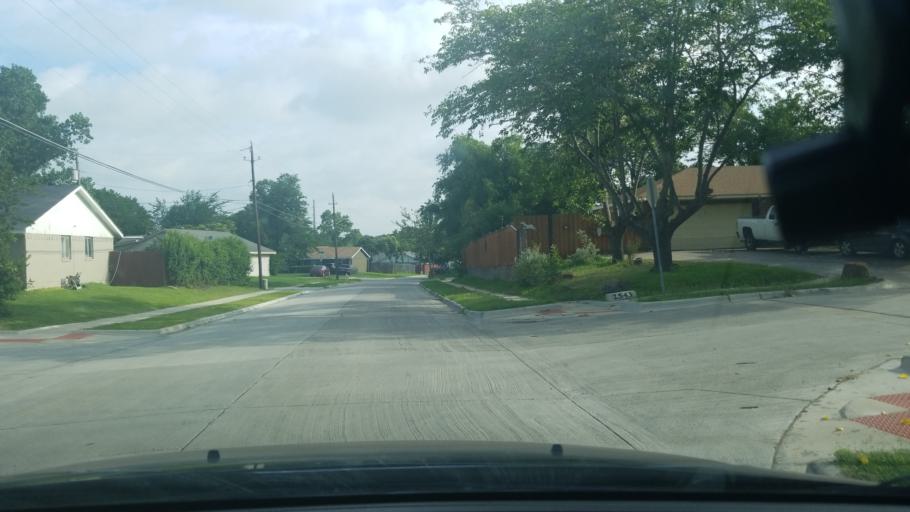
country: US
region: Texas
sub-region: Dallas County
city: Mesquite
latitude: 32.7724
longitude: -96.6401
